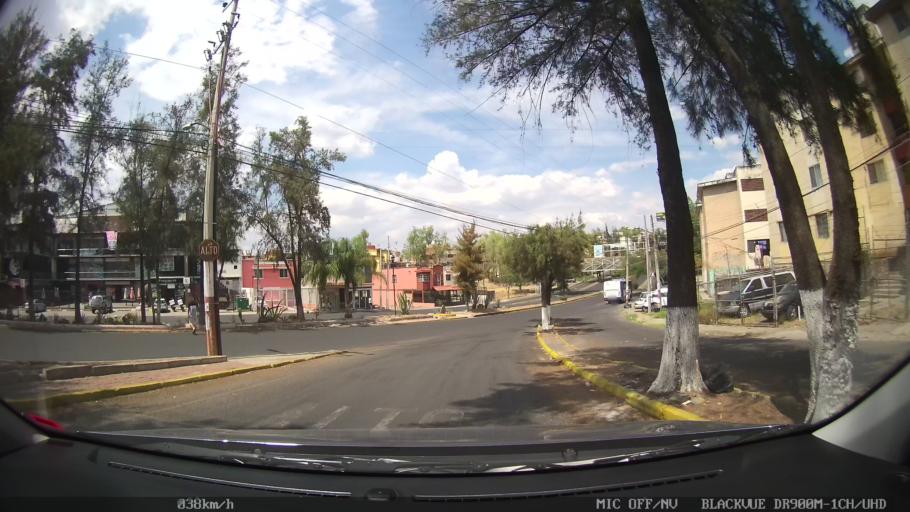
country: MX
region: Jalisco
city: Tonala
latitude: 20.6265
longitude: -103.2560
